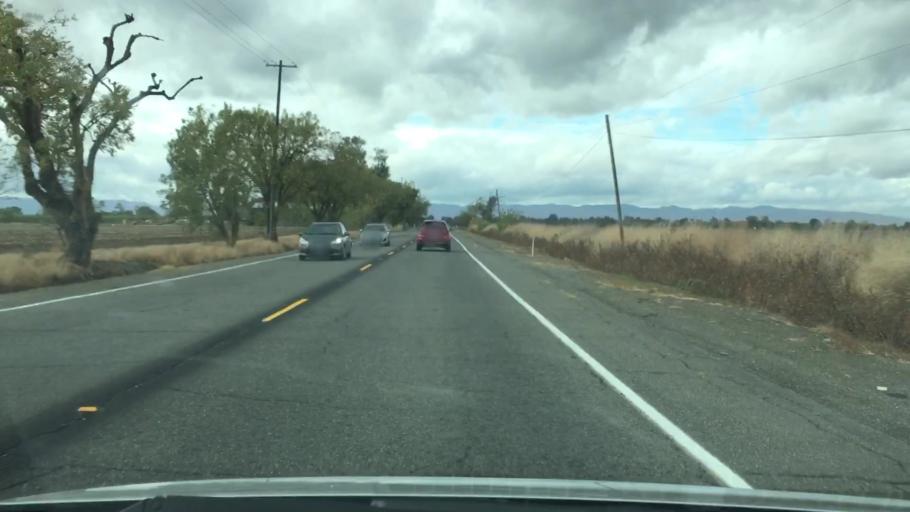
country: US
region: California
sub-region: Yolo County
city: Davis
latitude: 38.5616
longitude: -121.8275
